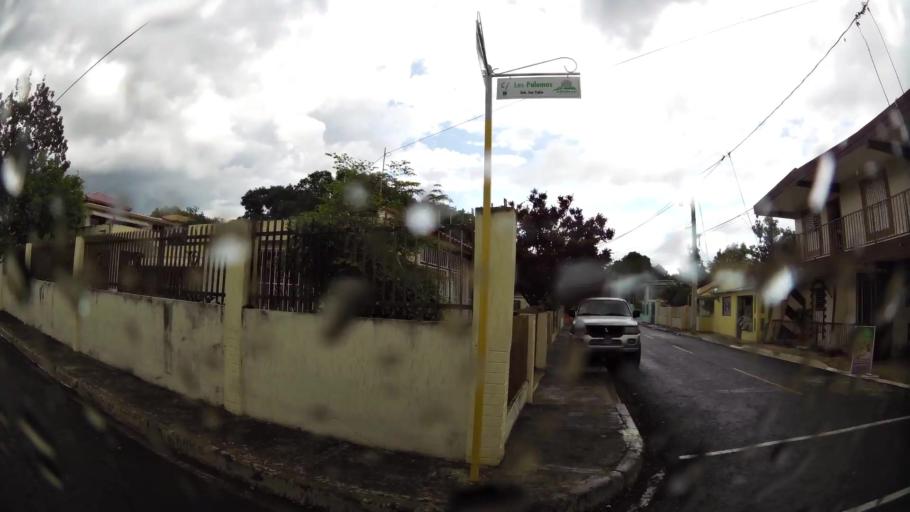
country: DO
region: Monsenor Nouel
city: Bonao
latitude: 18.9495
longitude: -70.4056
